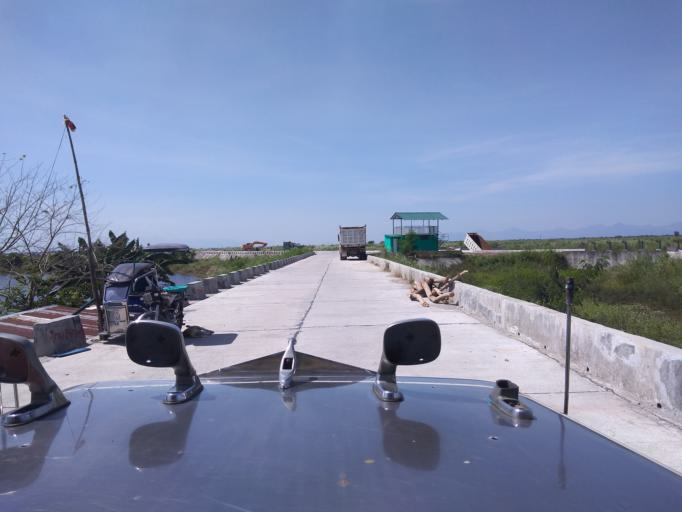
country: PH
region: Central Luzon
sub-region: Province of Pampanga
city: Minalin
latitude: 14.9804
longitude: 120.6844
